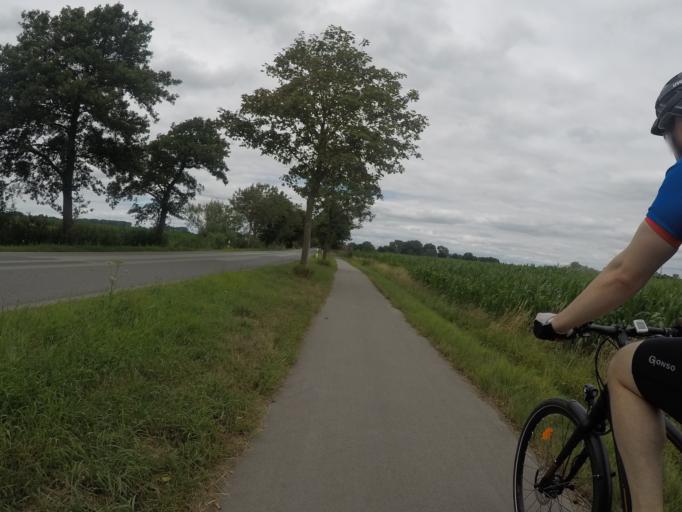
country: DE
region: Lower Saxony
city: Himmelpforten
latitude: 53.6415
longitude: 9.2971
